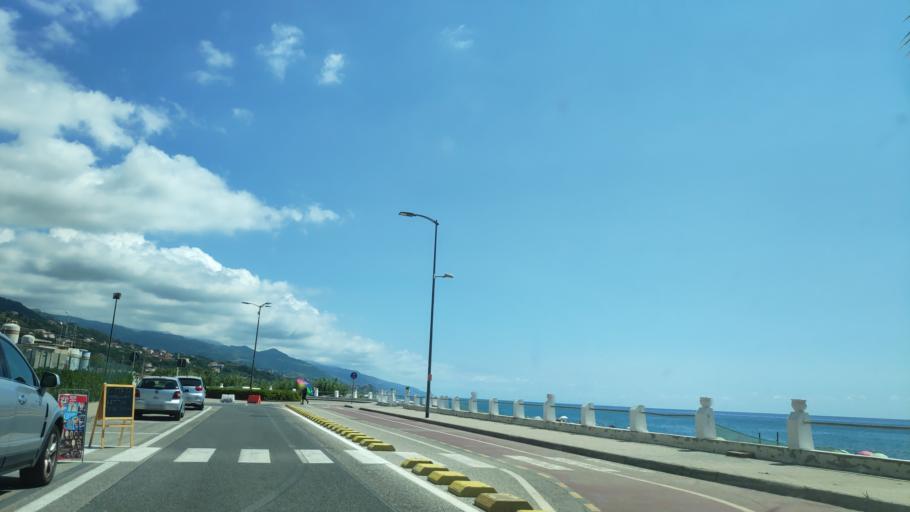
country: IT
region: Calabria
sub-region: Provincia di Cosenza
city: Paola
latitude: 39.3544
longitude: 16.0340
